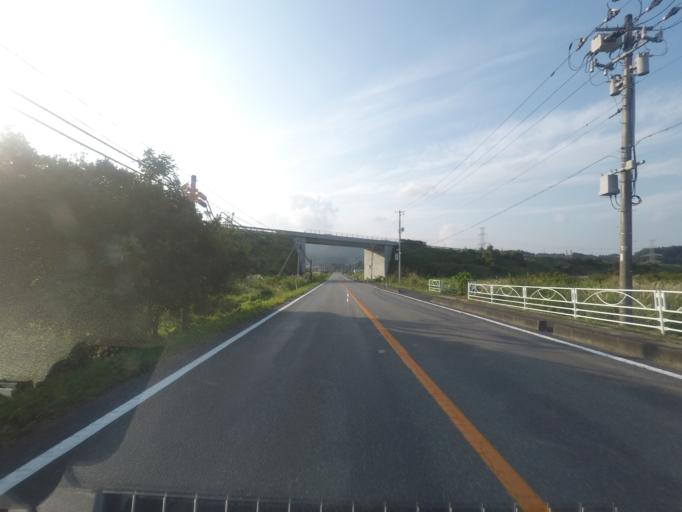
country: JP
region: Fukushima
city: Namie
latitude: 37.5039
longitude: 140.9435
